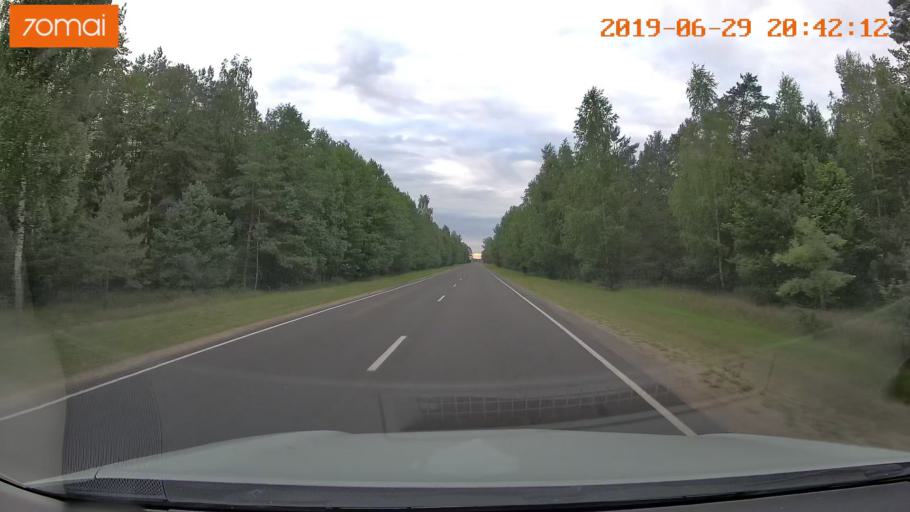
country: BY
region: Brest
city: Hantsavichy
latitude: 52.5948
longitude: 26.3296
